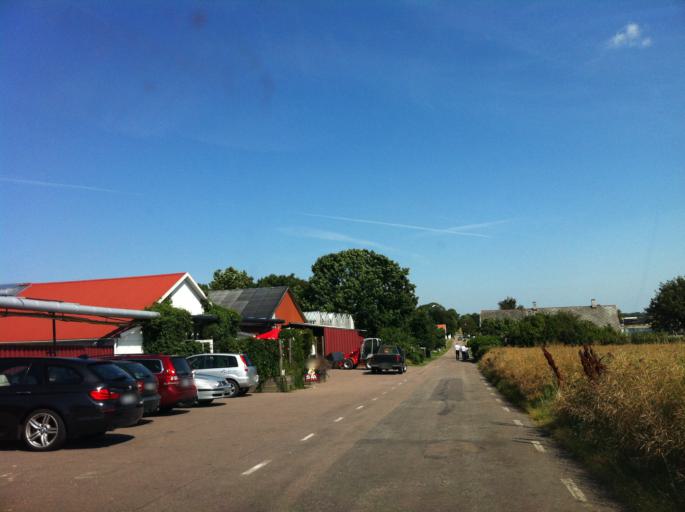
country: SE
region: Skane
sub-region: Helsingborg
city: Glumslov
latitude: 55.9534
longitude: 12.8325
